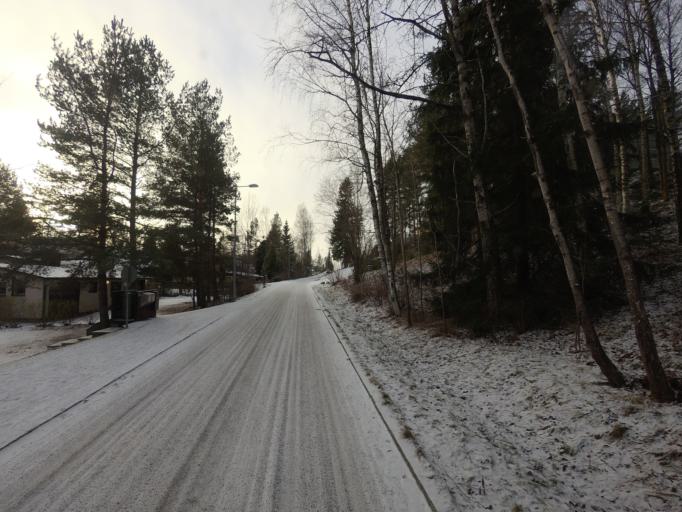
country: FI
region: Uusimaa
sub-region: Helsinki
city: Espoo
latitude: 60.1941
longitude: 24.6520
